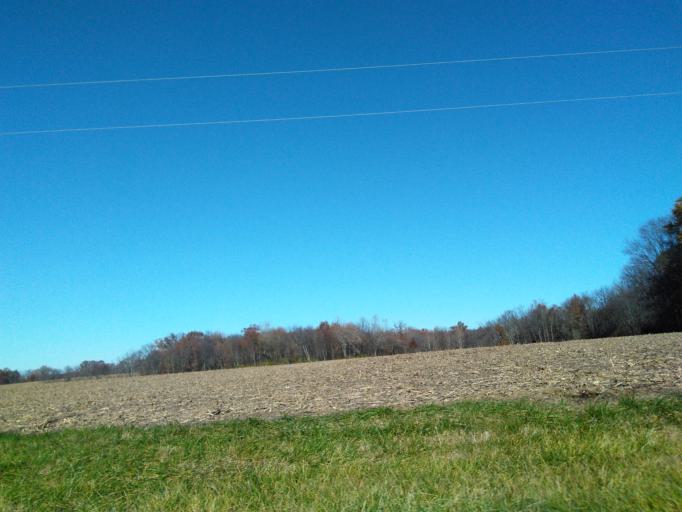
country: US
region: Illinois
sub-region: Madison County
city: Highland
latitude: 38.7334
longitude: -89.7174
